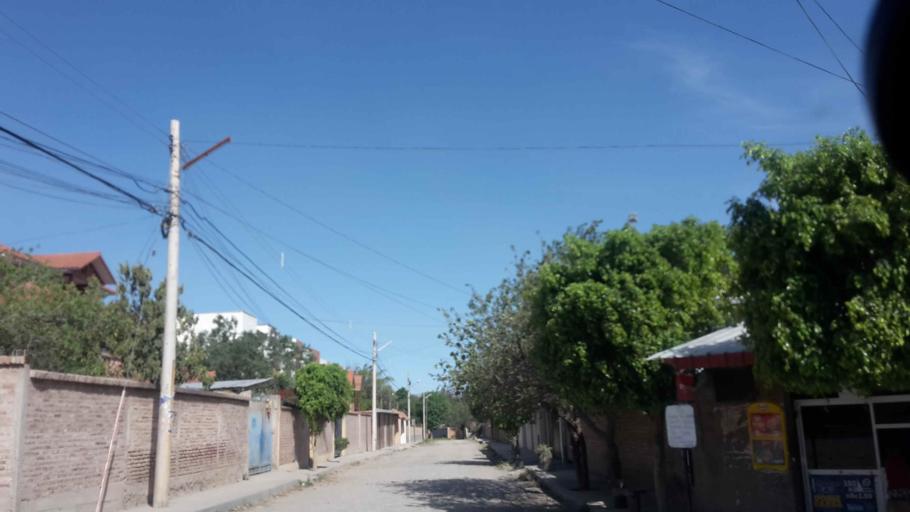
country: BO
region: Cochabamba
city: Cochabamba
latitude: -17.3490
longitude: -66.1992
